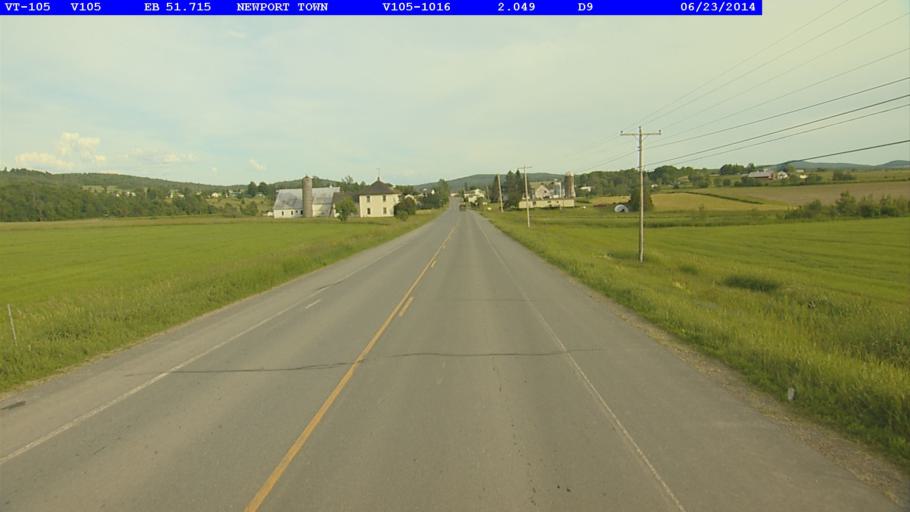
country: US
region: Vermont
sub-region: Orleans County
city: Newport
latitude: 44.9575
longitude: -72.3103
